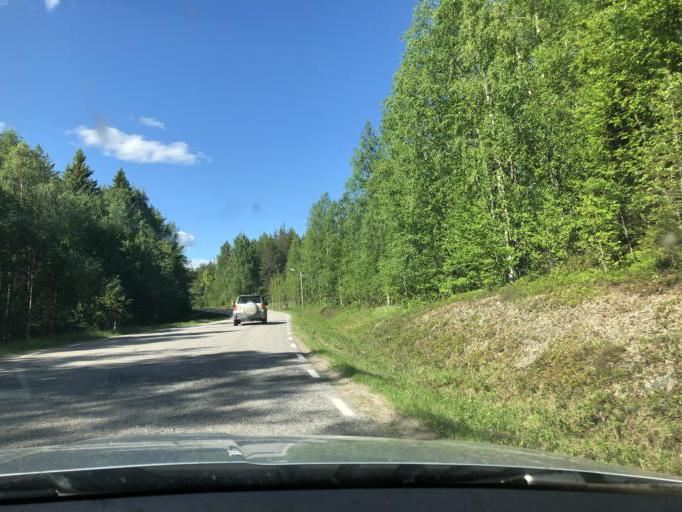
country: SE
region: Norrbotten
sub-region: Kalix Kommun
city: Kalix
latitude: 66.0013
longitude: 23.1424
